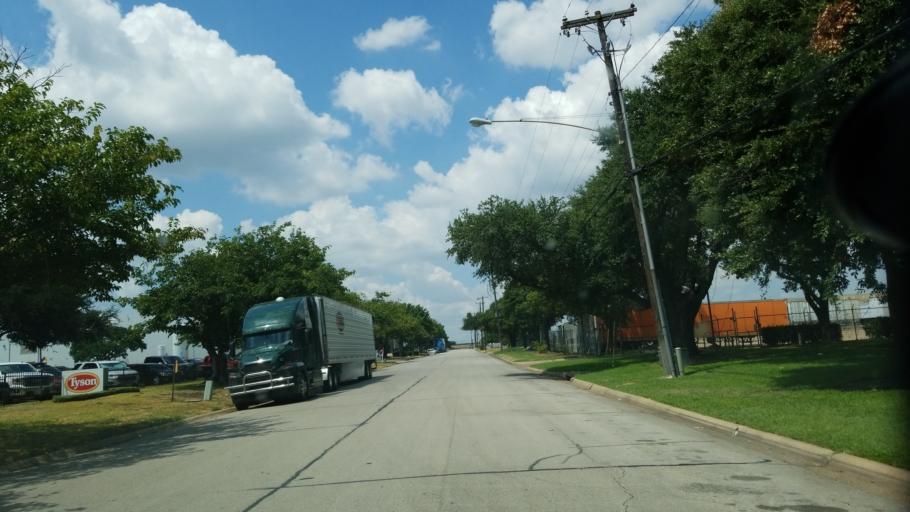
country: US
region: Texas
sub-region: Dallas County
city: Duncanville
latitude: 32.6852
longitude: -96.8871
